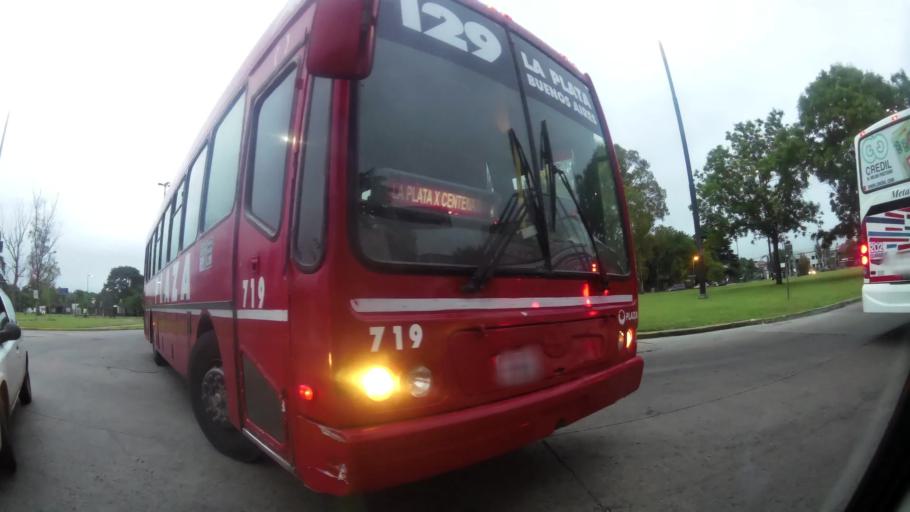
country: AR
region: Buenos Aires
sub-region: Partido de La Plata
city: La Plata
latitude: -34.9071
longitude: -57.9760
